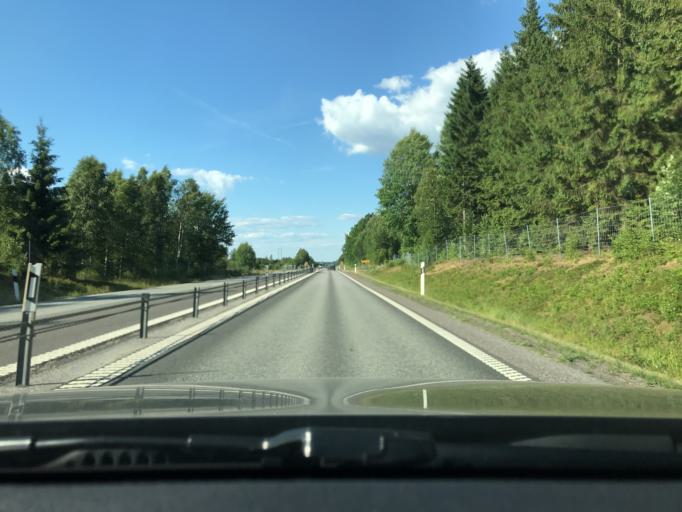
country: SE
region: Kronoberg
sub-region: Almhults Kommun
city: AElmhult
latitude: 56.4888
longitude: 14.1157
